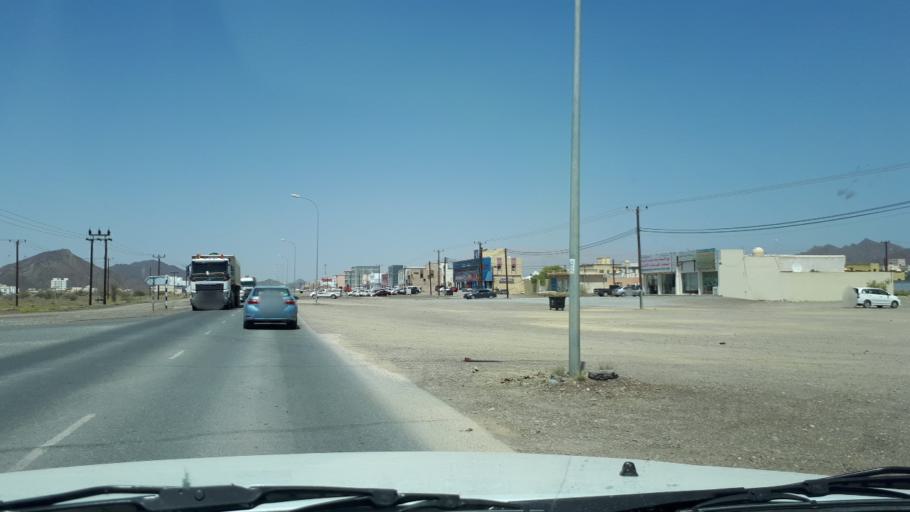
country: OM
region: Muhafazat ad Dakhiliyah
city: Bahla'
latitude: 22.9476
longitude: 57.2720
